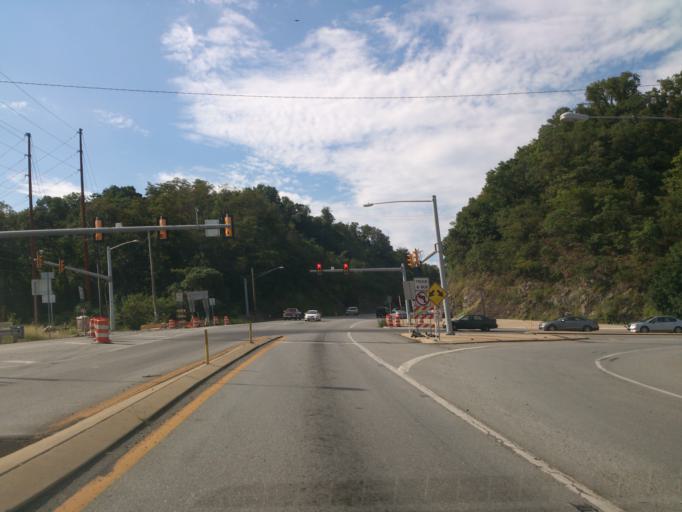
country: US
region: Pennsylvania
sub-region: Lancaster County
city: Columbia
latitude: 40.0386
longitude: -76.5101
